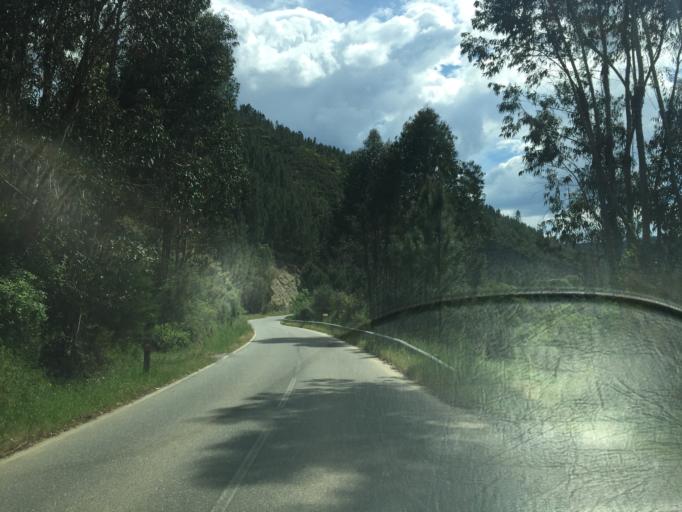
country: PT
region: Coimbra
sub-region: Pampilhosa da Serra
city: Pampilhosa da Serra
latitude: 40.0596
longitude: -7.7982
